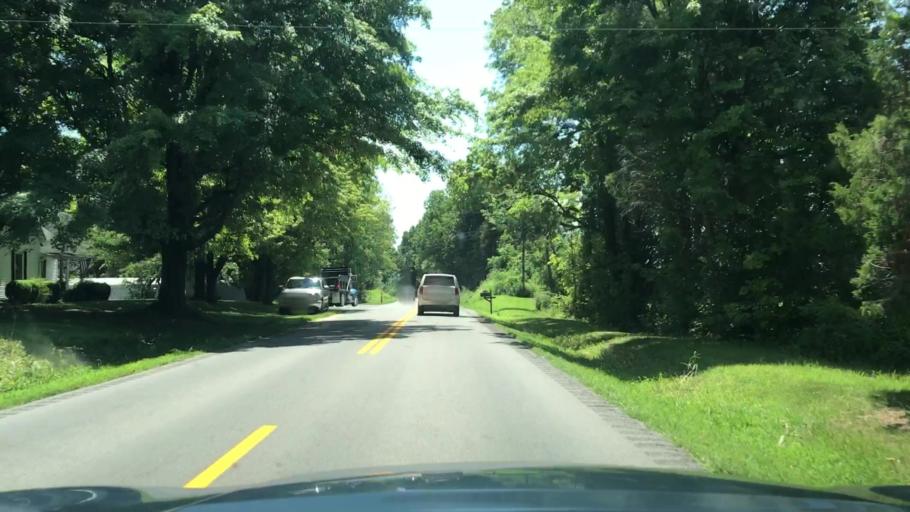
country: US
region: Kentucky
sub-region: Christian County
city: Hopkinsville
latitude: 36.8973
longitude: -87.4508
